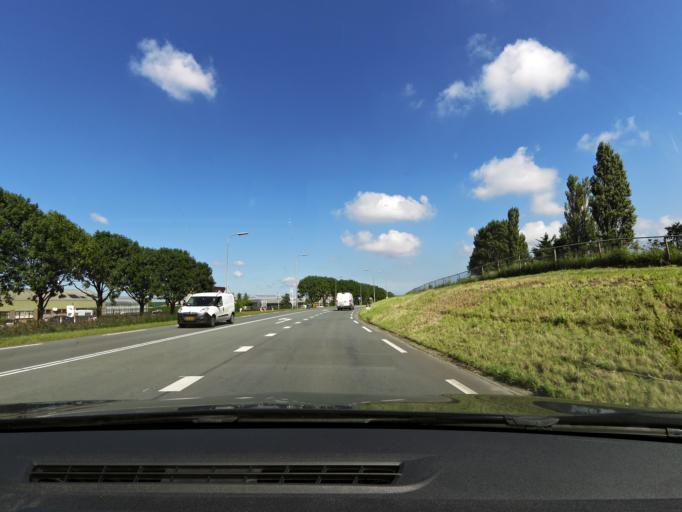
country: NL
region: North Holland
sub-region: Gemeente Aalsmeer
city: Aalsmeer
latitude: 52.2347
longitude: 4.7724
